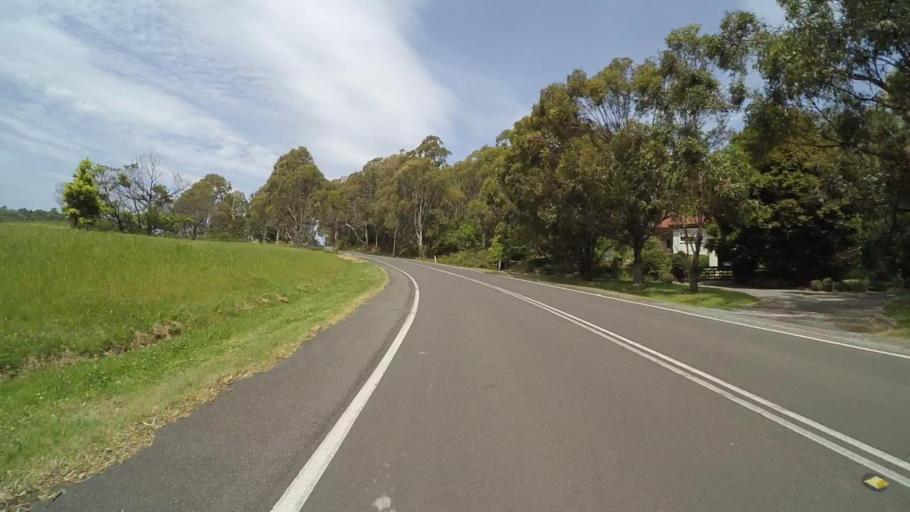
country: AU
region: New South Wales
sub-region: Shellharbour
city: Albion Park Rail
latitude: -34.5955
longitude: 150.7838
